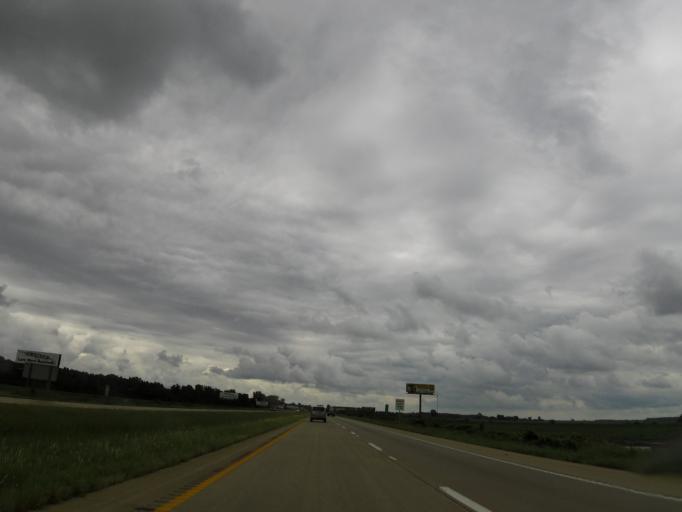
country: US
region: Missouri
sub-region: Mississippi County
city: Charleston
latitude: 36.9273
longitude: -89.3112
